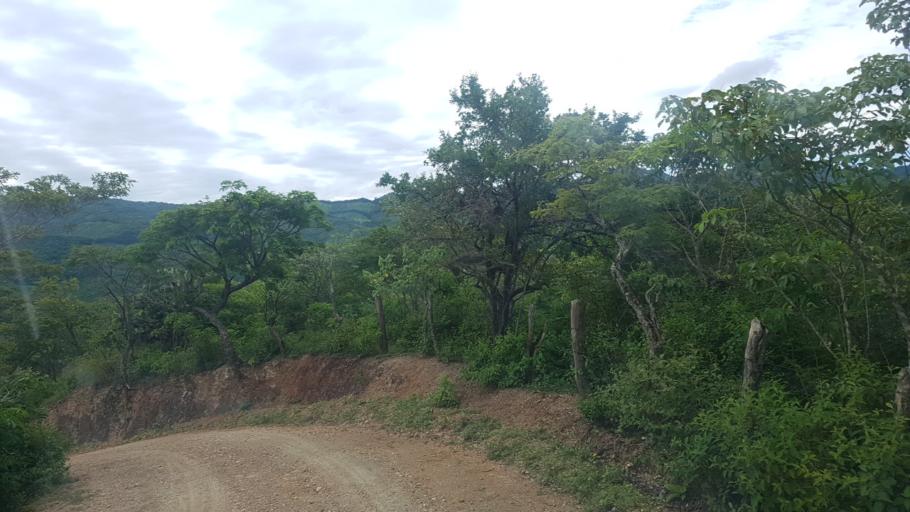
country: NI
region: Nueva Segovia
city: Mozonte
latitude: 13.5906
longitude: -86.4121
